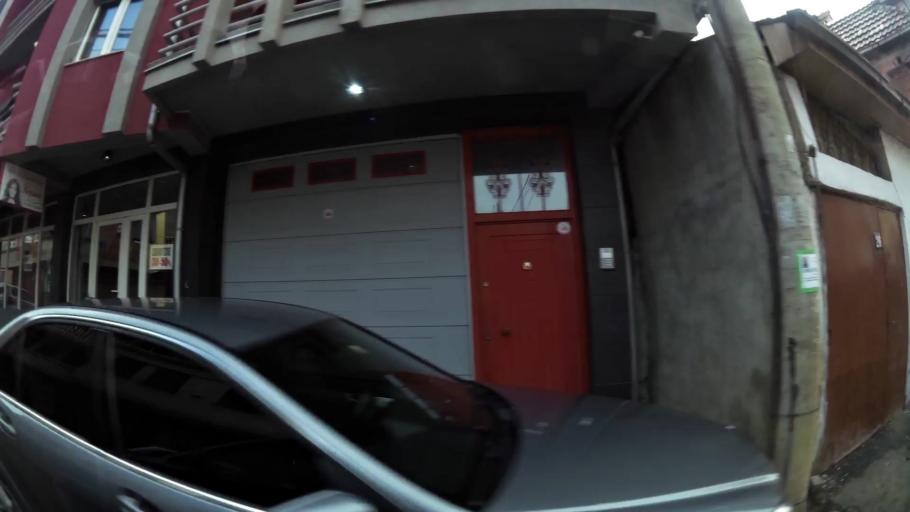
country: XK
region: Pristina
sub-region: Komuna e Prishtines
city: Pristina
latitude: 42.6656
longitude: 21.1705
